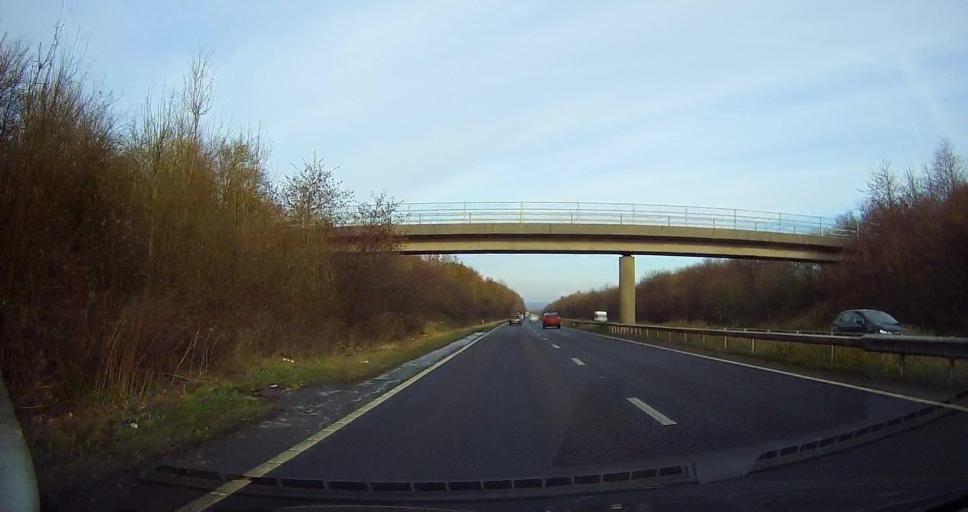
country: GB
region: England
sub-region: West Sussex
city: Hurstpierpoint
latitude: 50.9392
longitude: -0.1953
